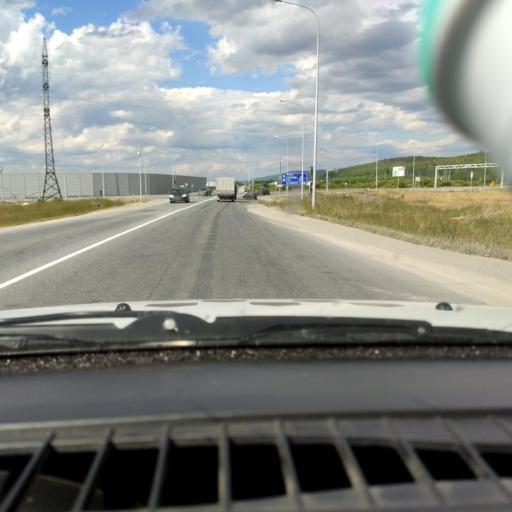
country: RU
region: Chelyabinsk
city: Miass
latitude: 54.9431
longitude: 60.0503
